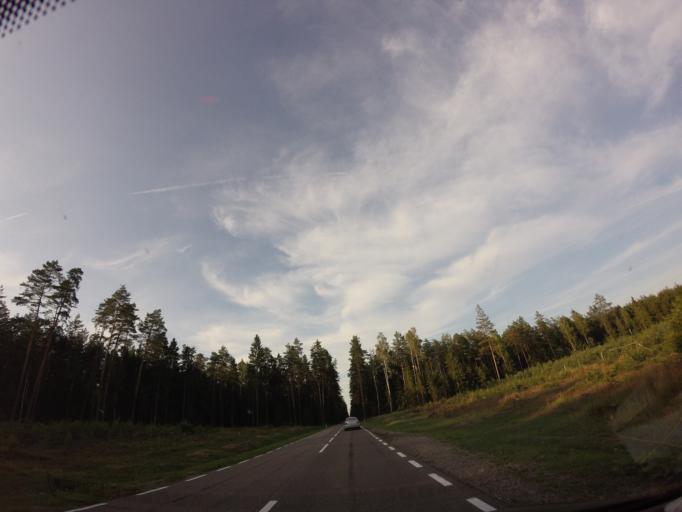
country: PL
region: Podlasie
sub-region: Powiat augustowski
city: Augustow
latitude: 53.8760
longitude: 23.1024
